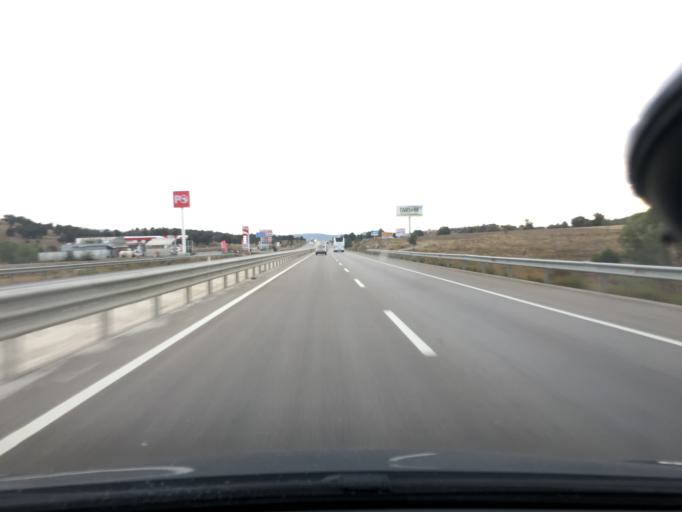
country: TR
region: Afyonkarahisar
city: Sincanli
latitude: 38.6537
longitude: 30.3188
